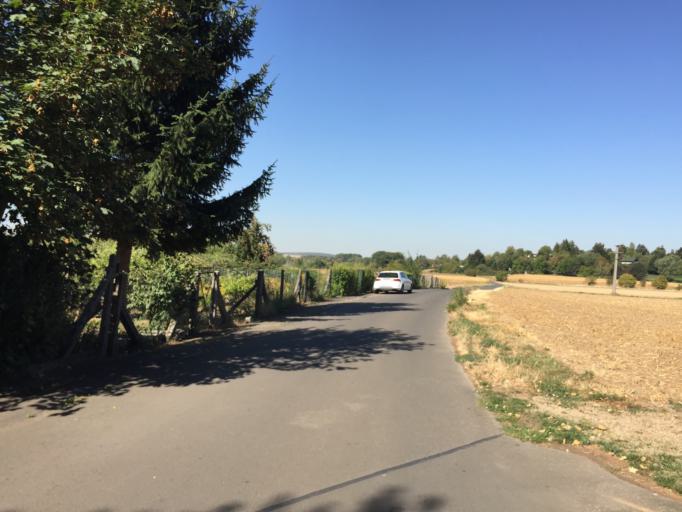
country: DE
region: Hesse
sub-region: Regierungsbezirk Giessen
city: Hungen
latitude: 50.4447
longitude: 8.9216
